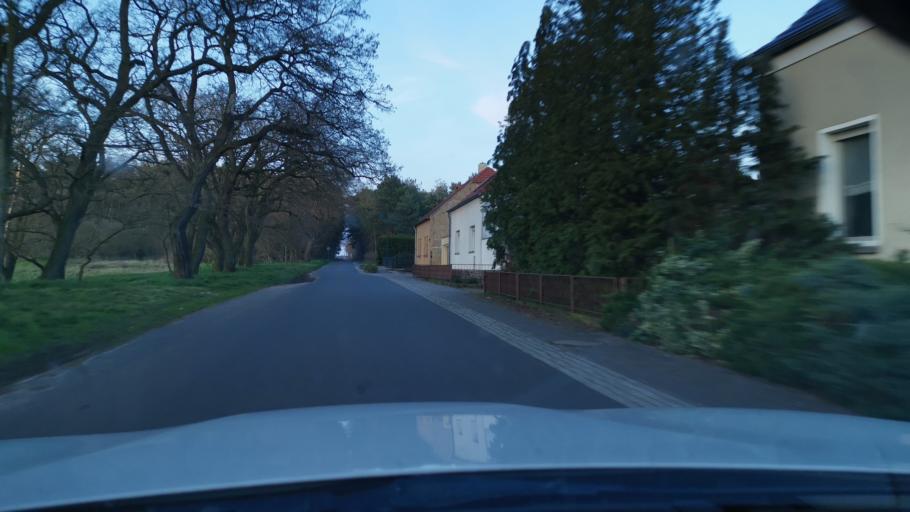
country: DE
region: Saxony-Anhalt
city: Zahna
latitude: 51.8905
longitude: 12.8208
